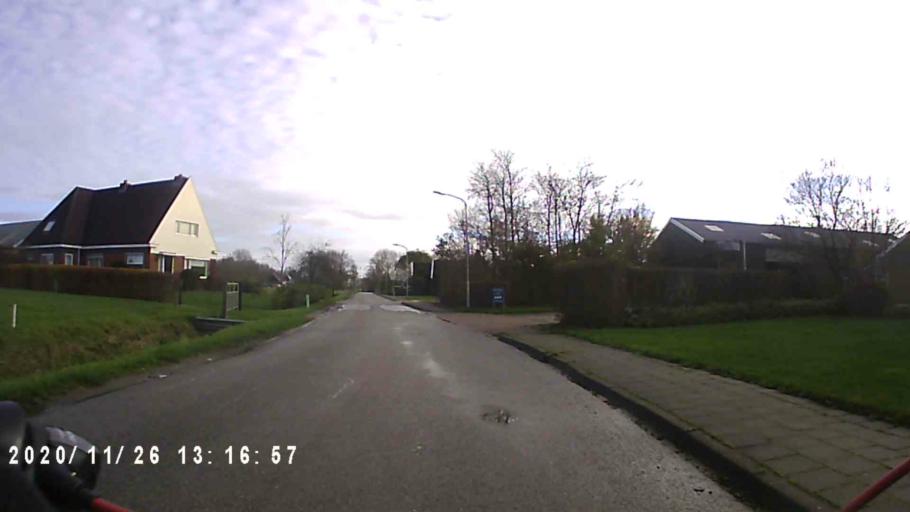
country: NL
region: Groningen
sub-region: Gemeente Appingedam
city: Appingedam
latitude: 53.3574
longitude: 6.8794
